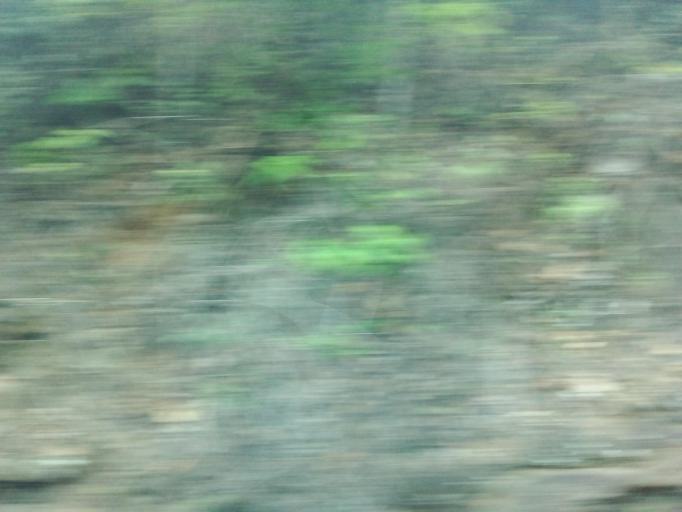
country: BR
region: Minas Gerais
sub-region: Nova Era
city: Nova Era
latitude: -19.7209
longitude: -42.9666
